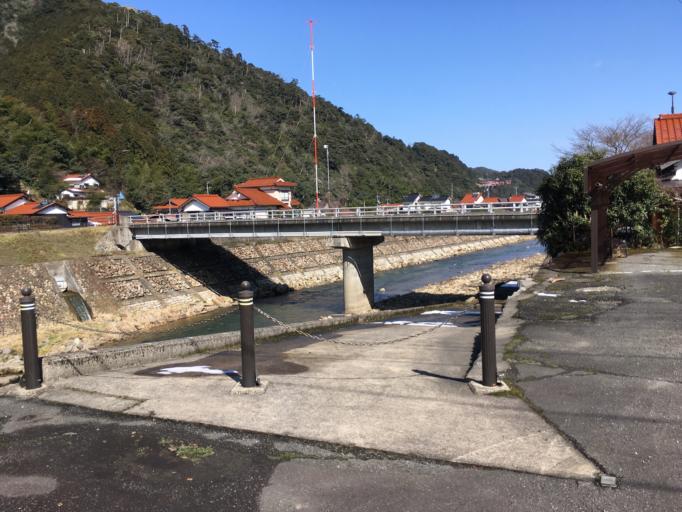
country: JP
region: Shimane
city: Masuda
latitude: 34.4547
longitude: 131.7666
